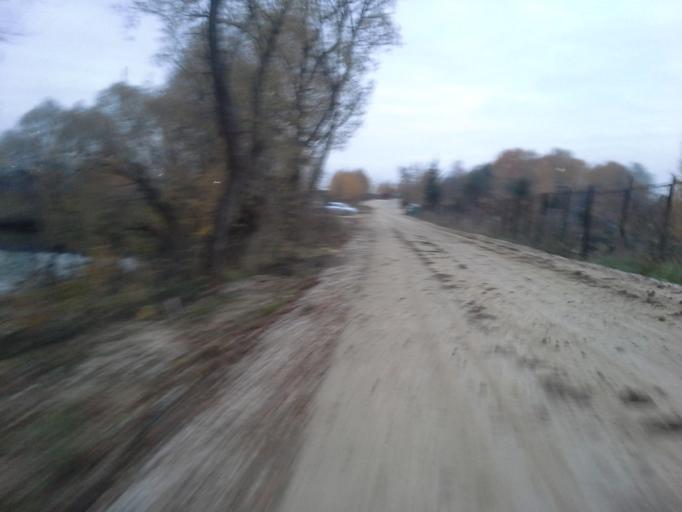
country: RU
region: Moskovskaya
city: Kommunarka
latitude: 55.5466
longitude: 37.4732
